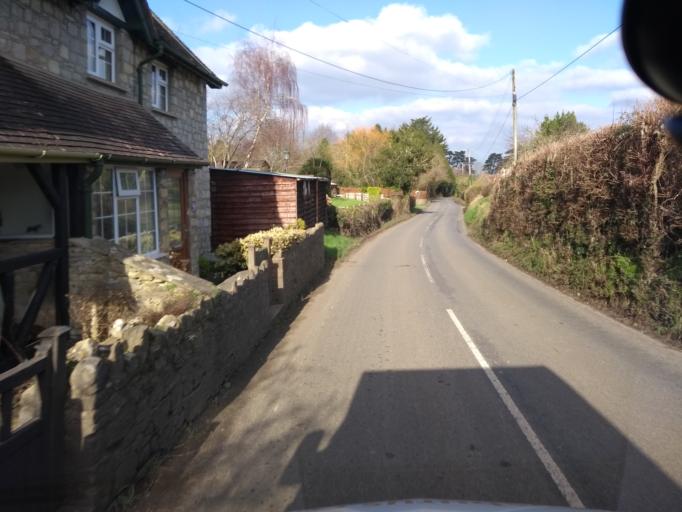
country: GB
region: England
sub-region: Somerset
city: Creech Saint Michael
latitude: 50.9771
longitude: -3.0558
